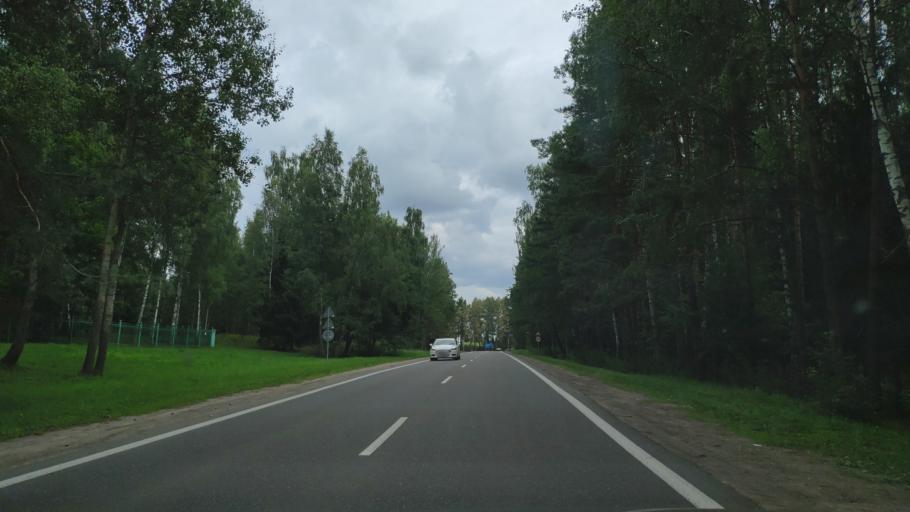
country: BY
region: Minsk
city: Syomkava
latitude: 53.9918
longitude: 27.4670
